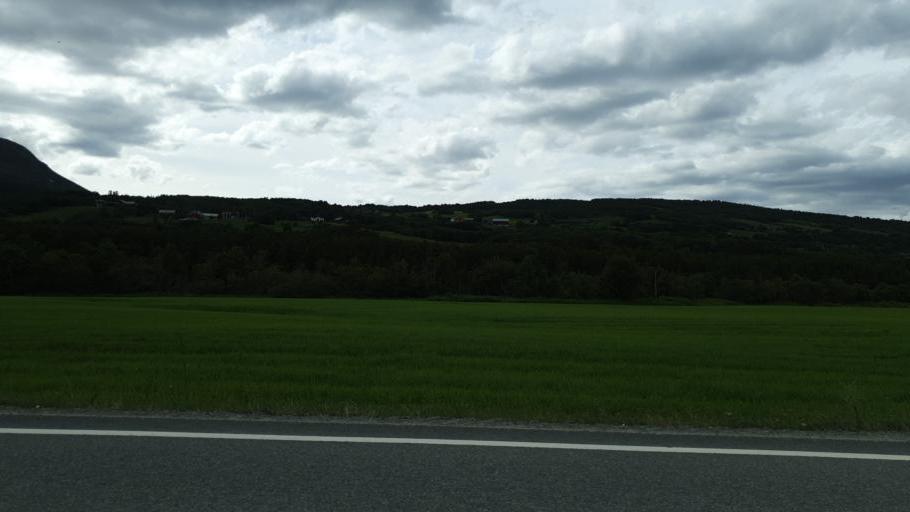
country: NO
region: Sor-Trondelag
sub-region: Oppdal
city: Oppdal
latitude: 62.5604
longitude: 9.6392
